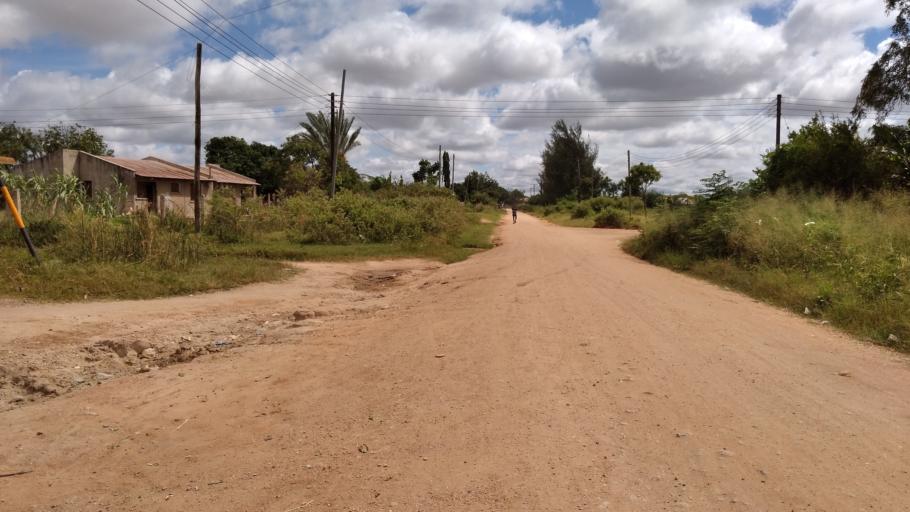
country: TZ
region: Dodoma
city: Dodoma
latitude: -6.1662
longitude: 35.7371
